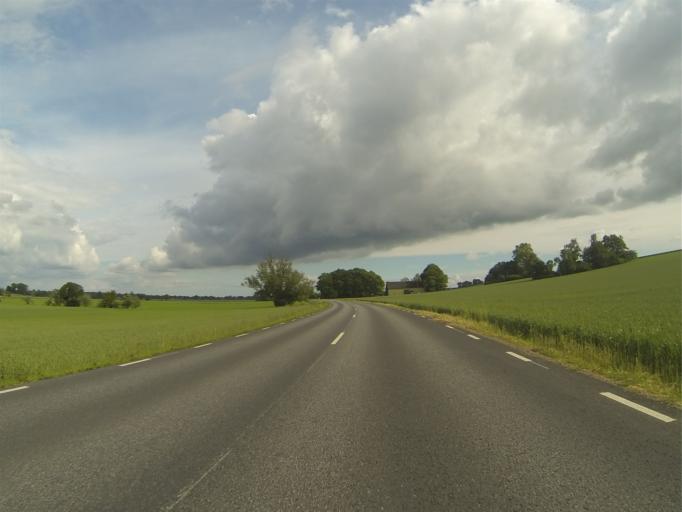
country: SE
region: Skane
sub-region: Eslovs Kommun
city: Eslov
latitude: 55.7570
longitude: 13.3189
